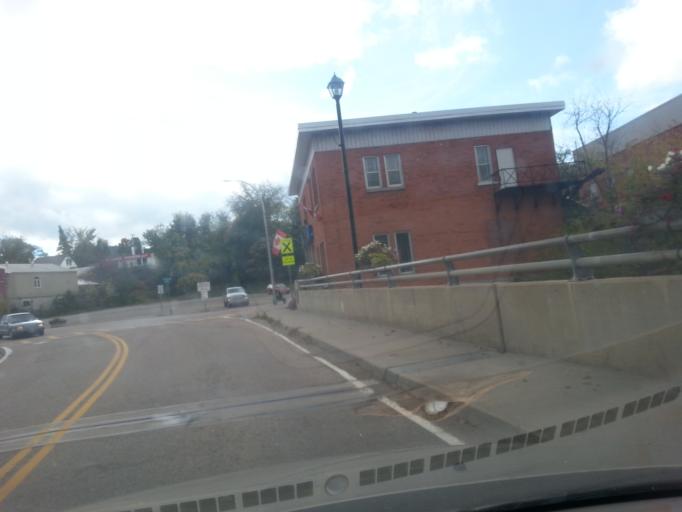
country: CA
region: Ontario
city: Pembroke
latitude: 45.5398
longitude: -77.1011
